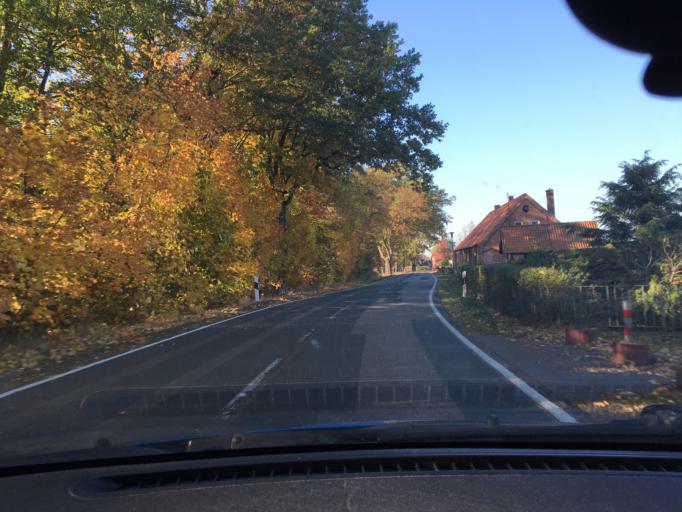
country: DE
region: Lower Saxony
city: Damnatz
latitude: 53.1686
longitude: 11.1702
